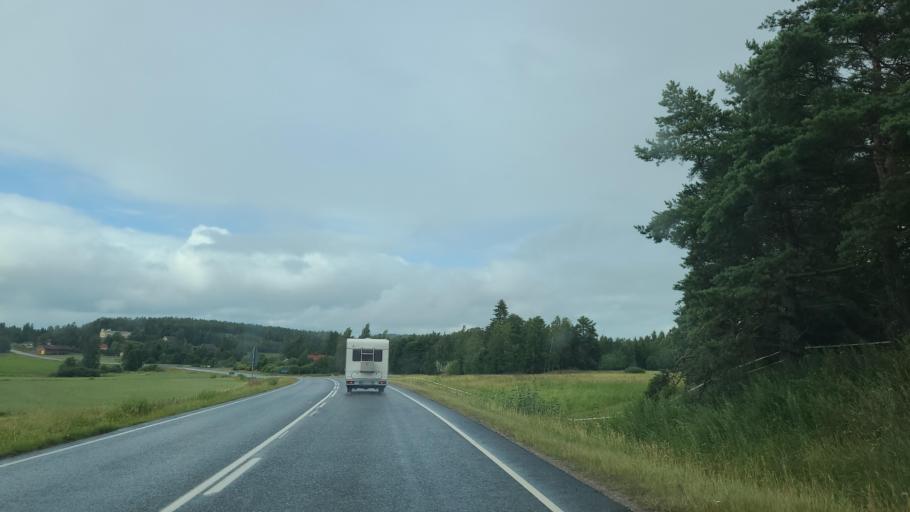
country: FI
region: Varsinais-Suomi
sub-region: Turku
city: Sauvo
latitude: 60.3282
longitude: 22.7142
